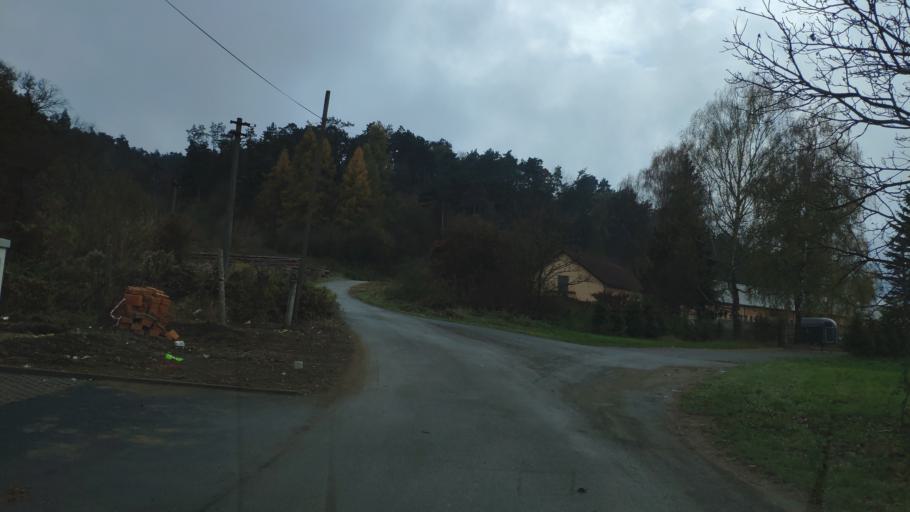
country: SK
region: Presovsky
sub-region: Okres Presov
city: Presov
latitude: 49.0324
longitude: 21.2037
